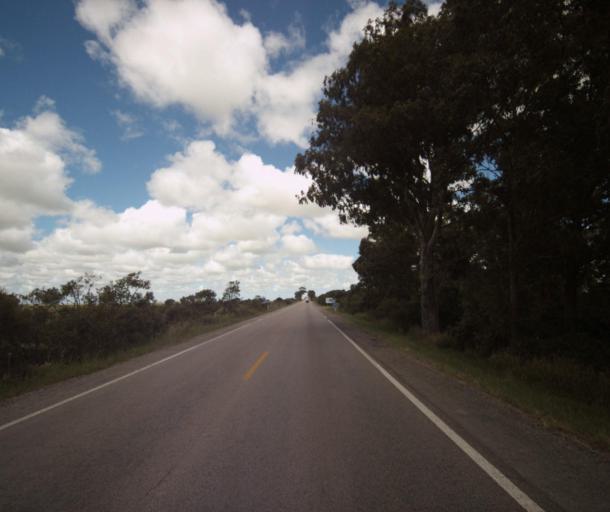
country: BR
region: Rio Grande do Sul
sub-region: Rio Grande
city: Rio Grande
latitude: -32.1846
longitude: -52.4273
